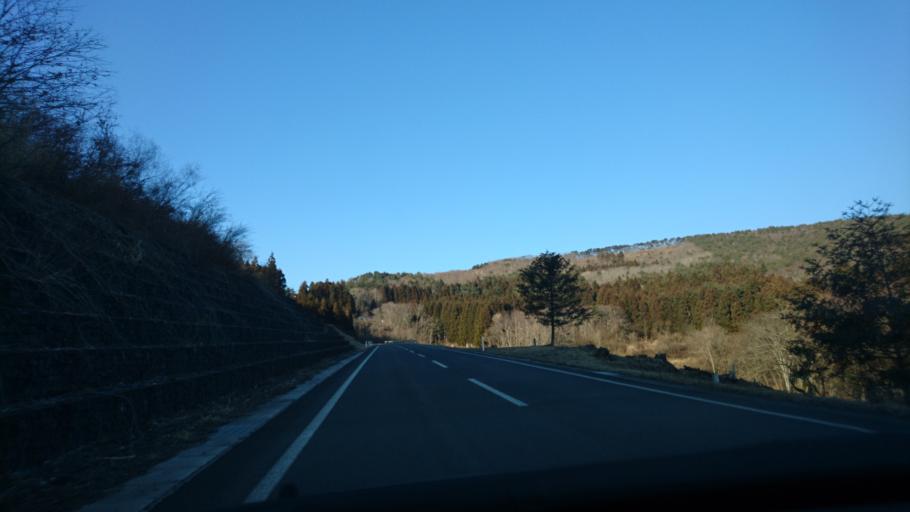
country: JP
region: Iwate
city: Ichinoseki
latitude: 38.8568
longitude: 141.3912
